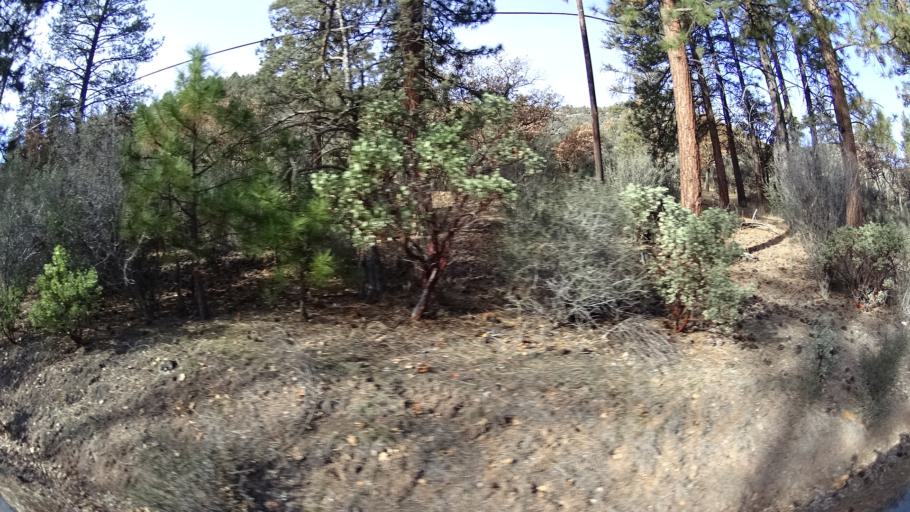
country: US
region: California
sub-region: Siskiyou County
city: Montague
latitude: 41.6082
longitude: -122.5773
